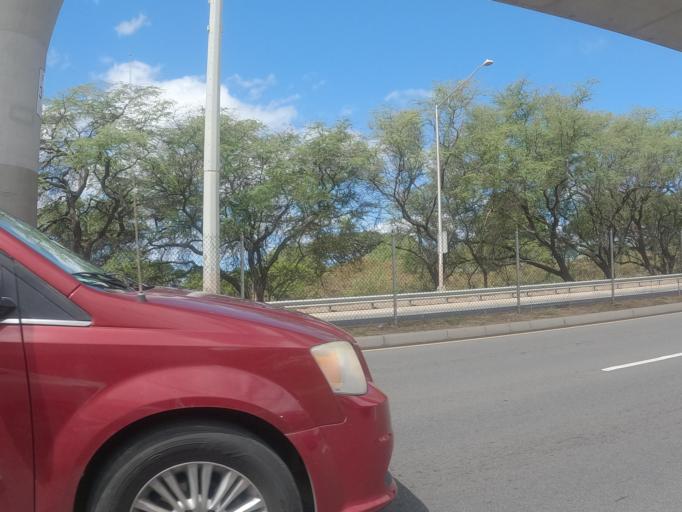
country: US
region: Hawaii
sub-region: Honolulu County
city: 'Aiea
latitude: 21.3785
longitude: -157.9359
